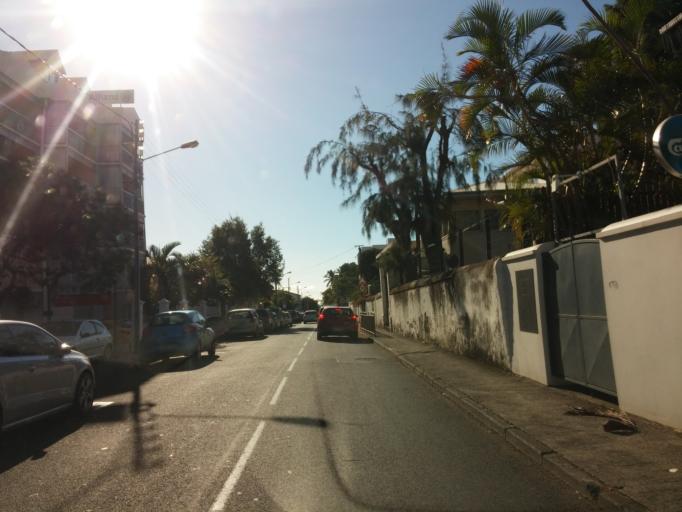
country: RE
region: Reunion
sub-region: Reunion
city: Saint-Denis
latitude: -20.8837
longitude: 55.4479
